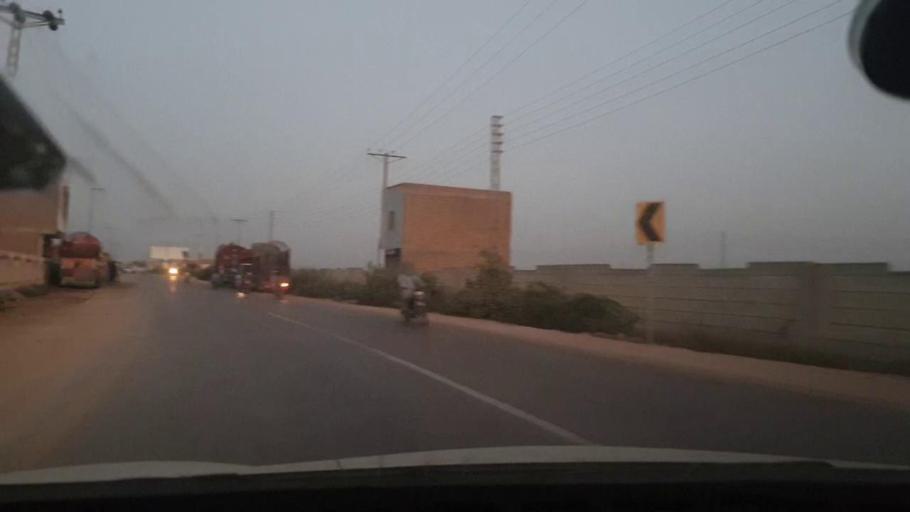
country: PK
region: Sindh
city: Tando Adam
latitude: 25.7477
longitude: 68.6450
